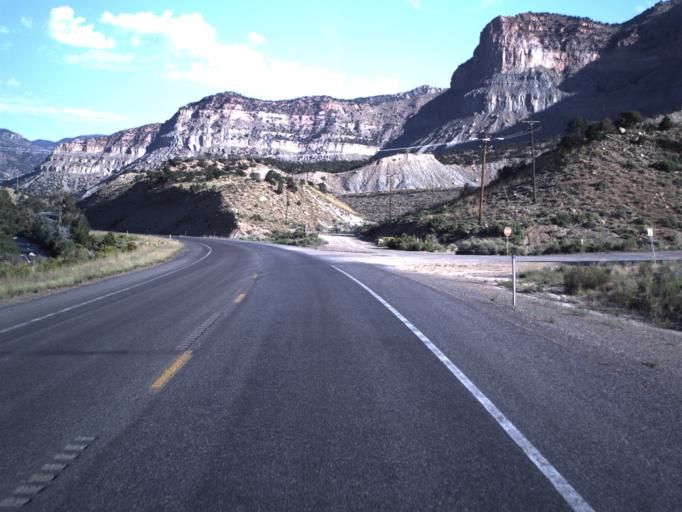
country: US
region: Utah
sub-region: Emery County
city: Huntington
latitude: 39.3732
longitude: -111.0626
